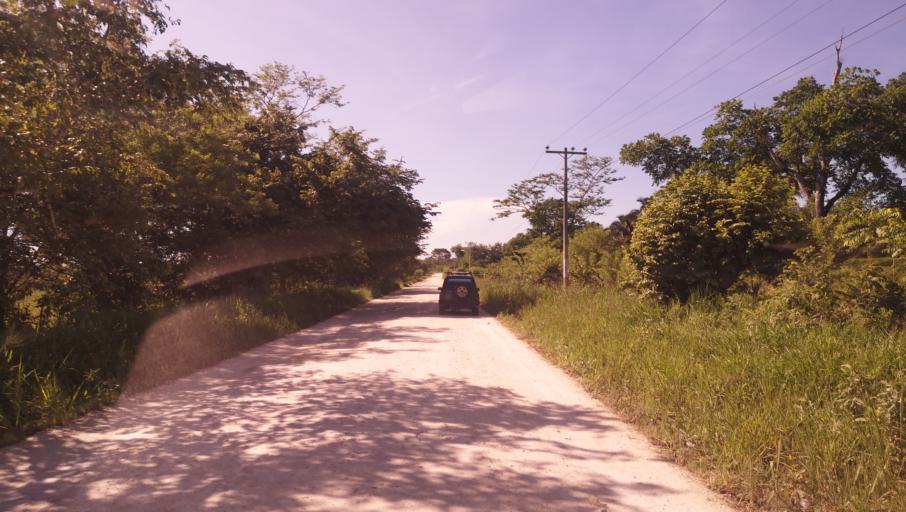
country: GT
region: Peten
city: Dolores
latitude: 16.7182
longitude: -89.3706
